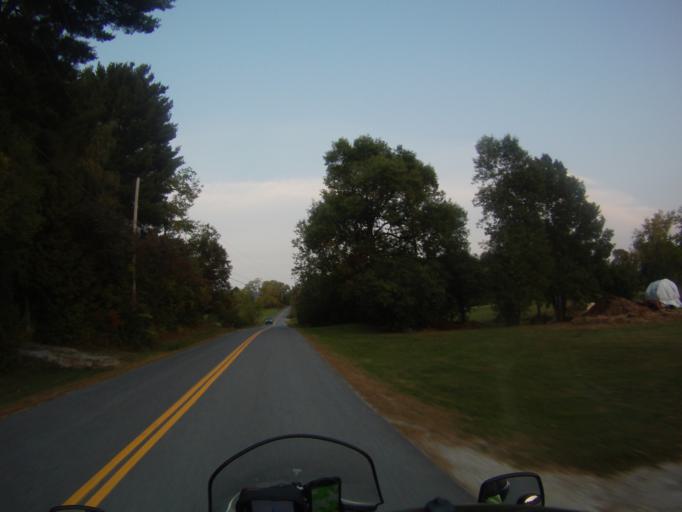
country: US
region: Vermont
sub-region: Rutland County
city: Brandon
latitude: 43.7927
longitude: -73.1054
